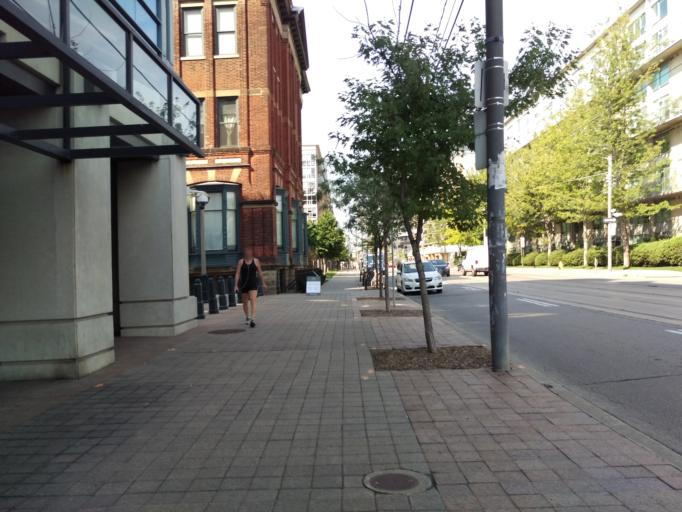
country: CA
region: Ontario
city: Toronto
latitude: 43.6419
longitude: -79.4123
